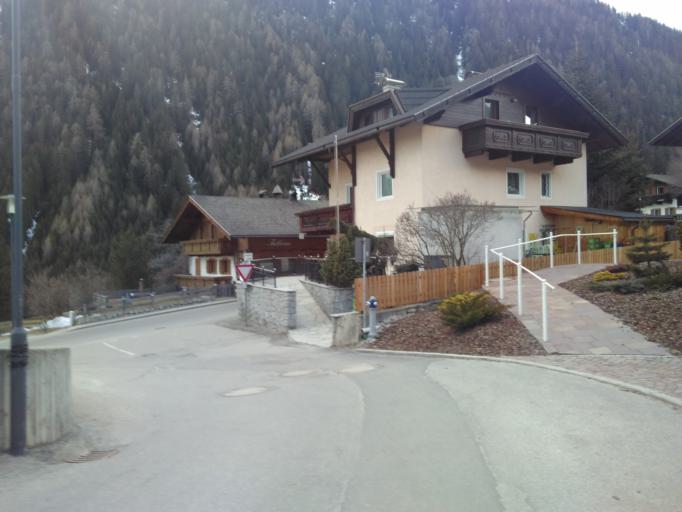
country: IT
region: Trentino-Alto Adige
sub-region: Bolzano
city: Fortezza
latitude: 46.8398
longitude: 11.6270
